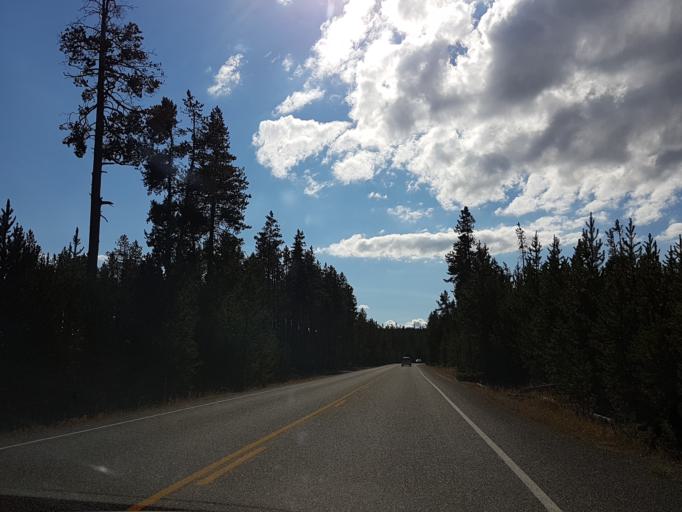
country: US
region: Montana
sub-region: Gallatin County
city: West Yellowstone
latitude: 44.6229
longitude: -110.8586
